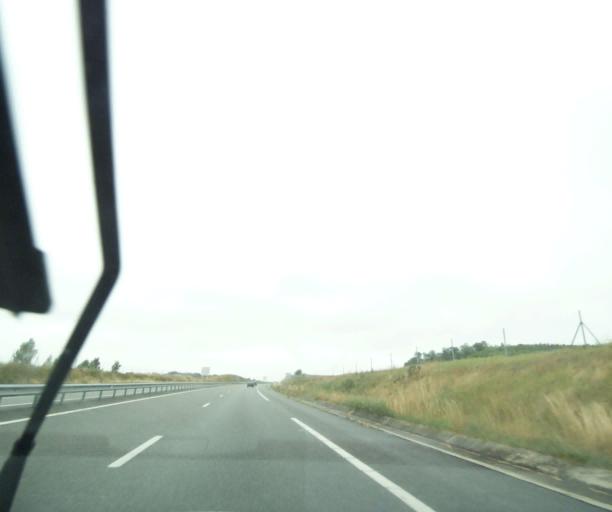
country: FR
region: Midi-Pyrenees
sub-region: Departement du Tarn
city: Le Garric
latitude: 44.0188
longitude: 2.1821
